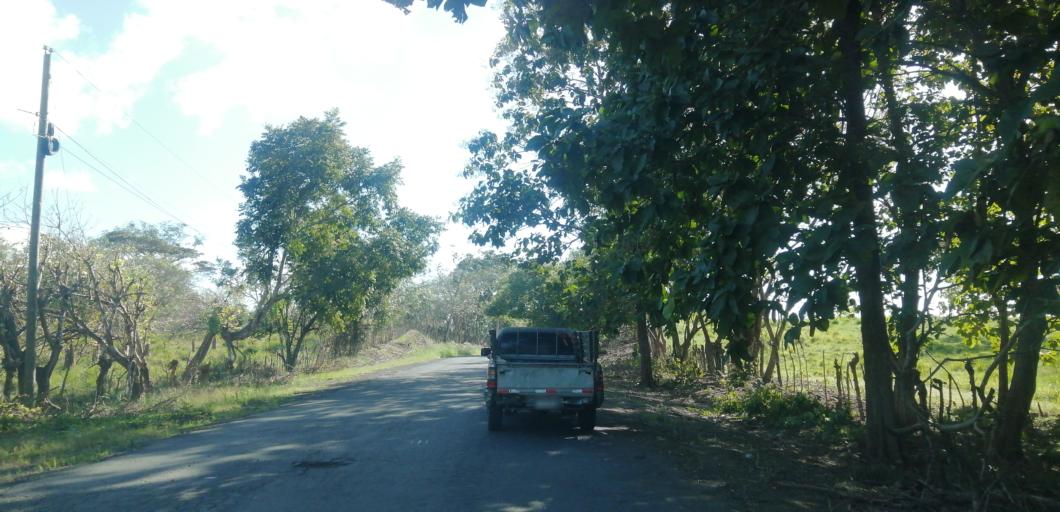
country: PA
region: Panama
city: Canita
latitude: 9.2184
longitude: -78.8405
